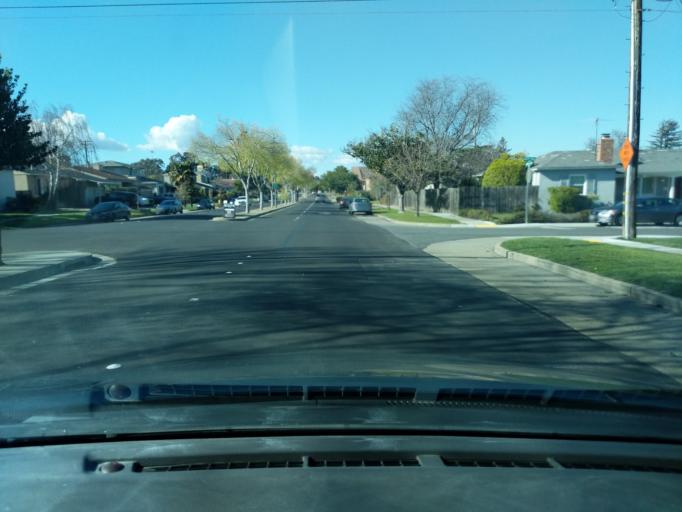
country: US
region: California
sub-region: San Mateo County
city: San Mateo
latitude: 37.5357
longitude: -122.3106
